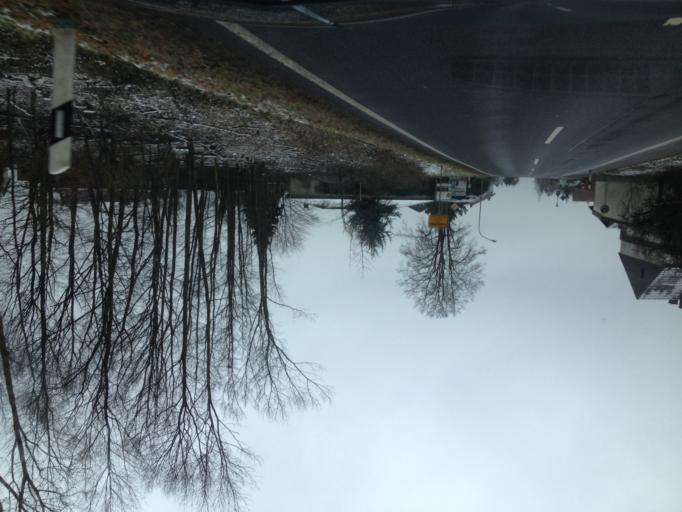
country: DE
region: Saarland
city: Bexbach
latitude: 49.3867
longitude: 7.2528
